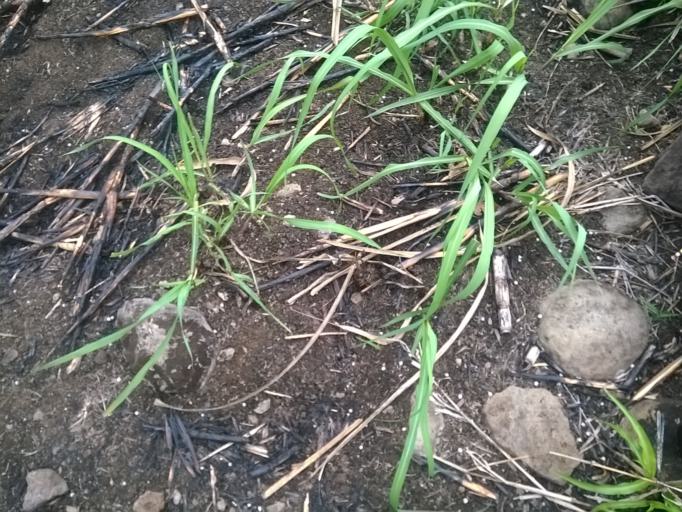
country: CR
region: Cartago
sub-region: Canton de Turrialba
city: La Suiza
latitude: 9.8749
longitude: -83.6352
